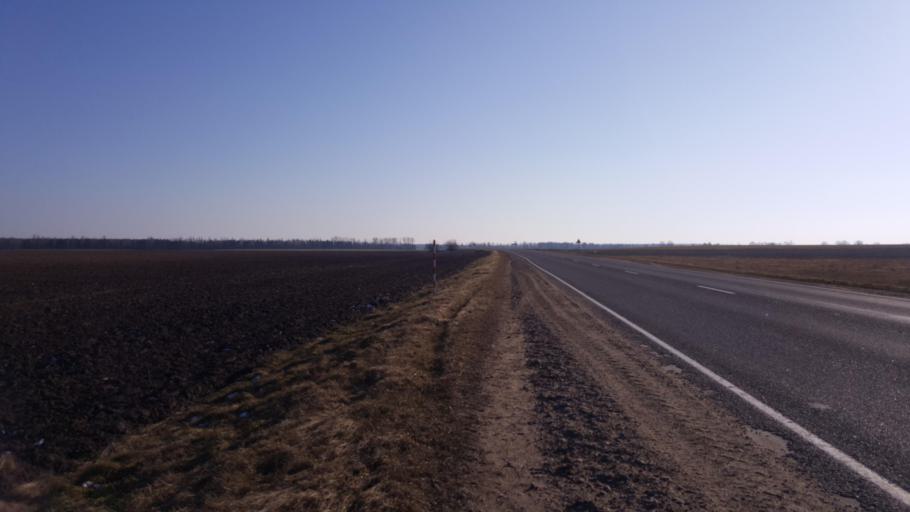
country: BY
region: Brest
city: Kamyanyets
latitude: 52.3844
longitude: 23.7879
